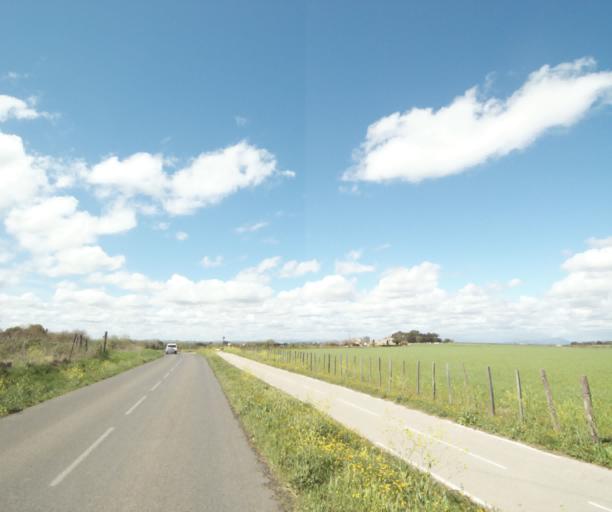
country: FR
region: Languedoc-Roussillon
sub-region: Departement de l'Herault
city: Lattes
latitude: 43.5596
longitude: 3.9273
